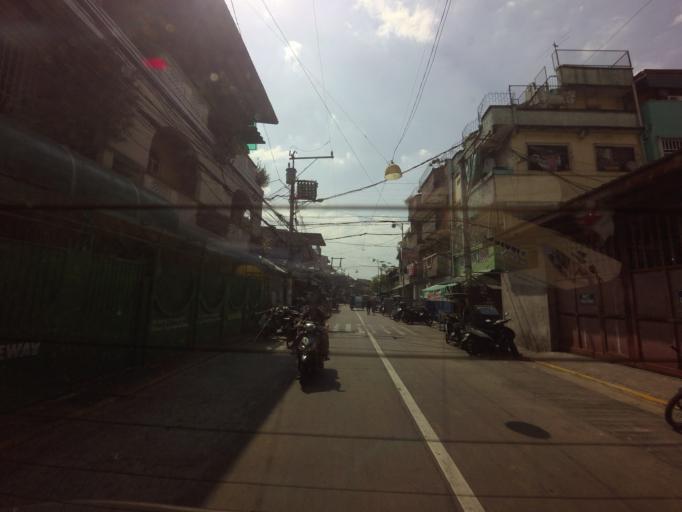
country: PH
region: Metro Manila
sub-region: City of Manila
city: Manila
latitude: 14.6160
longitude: 120.9663
